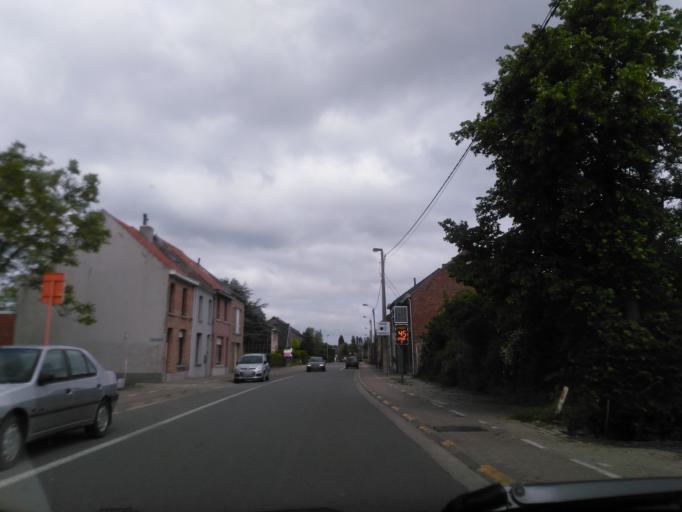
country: BE
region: Flanders
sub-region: Provincie Oost-Vlaanderen
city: Beveren
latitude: 51.2010
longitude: 4.2653
